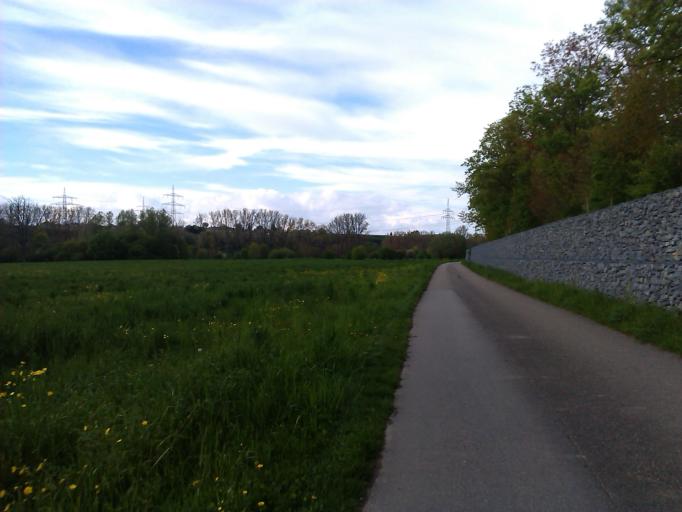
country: DE
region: Baden-Wuerttemberg
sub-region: Regierungsbezirk Stuttgart
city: Nordheim
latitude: 49.1069
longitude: 9.1532
